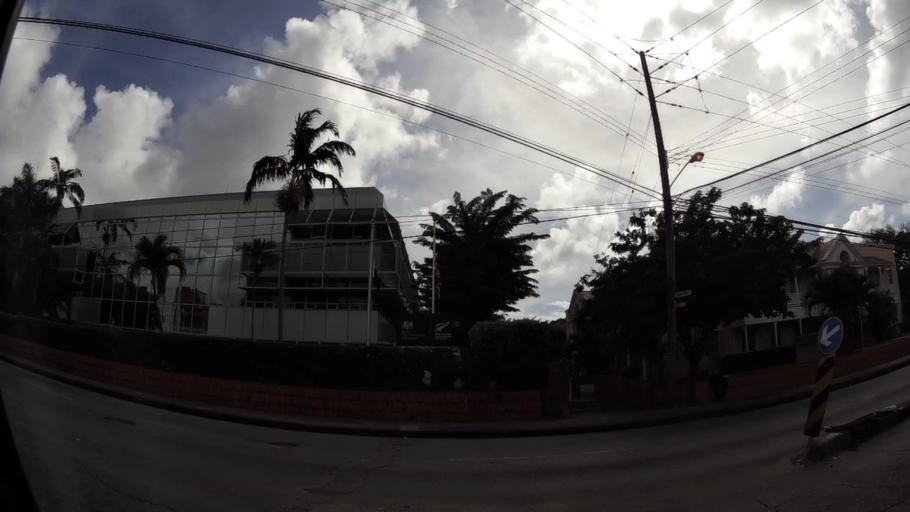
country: BB
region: Saint Michael
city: Bridgetown
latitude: 13.0928
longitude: -59.6034
